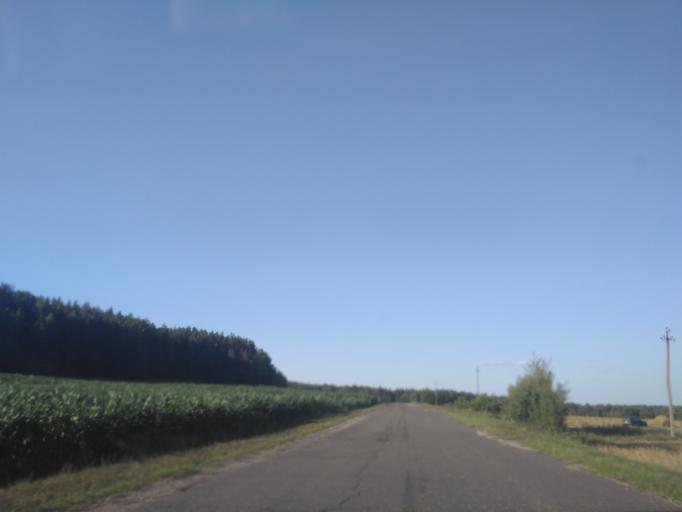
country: BY
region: Minsk
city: Horad Barysaw
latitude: 54.3838
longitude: 28.5723
